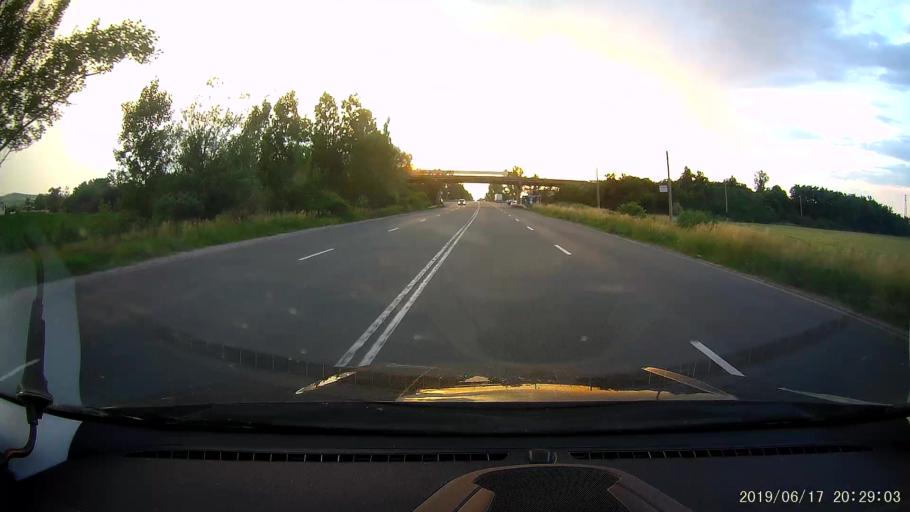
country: BG
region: Sofiya
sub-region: Obshtina Bozhurishte
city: Bozhurishte
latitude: 42.7830
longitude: 23.1683
